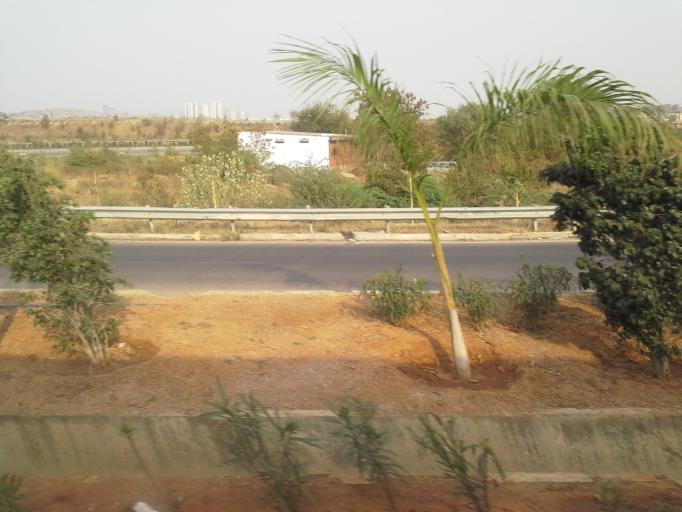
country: IN
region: Telangana
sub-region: Hyderabad
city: Hyderabad
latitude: 17.3951
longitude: 78.3488
